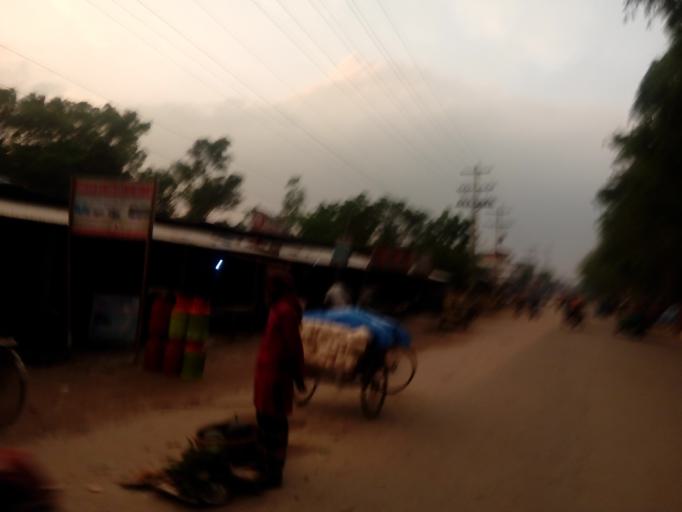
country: BD
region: Rajshahi
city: Shahzadpur
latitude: 24.2942
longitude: 89.6973
